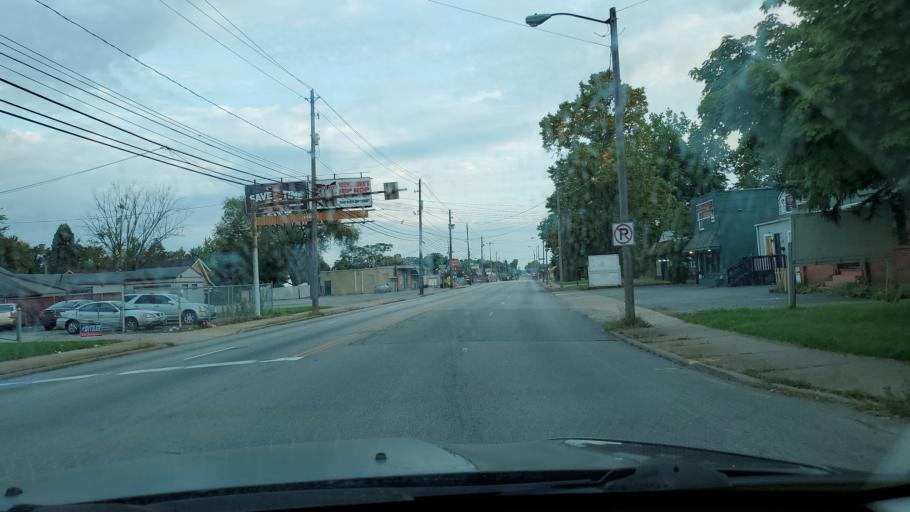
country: US
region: Ohio
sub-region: Mahoning County
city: Youngstown
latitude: 41.0623
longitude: -80.6461
